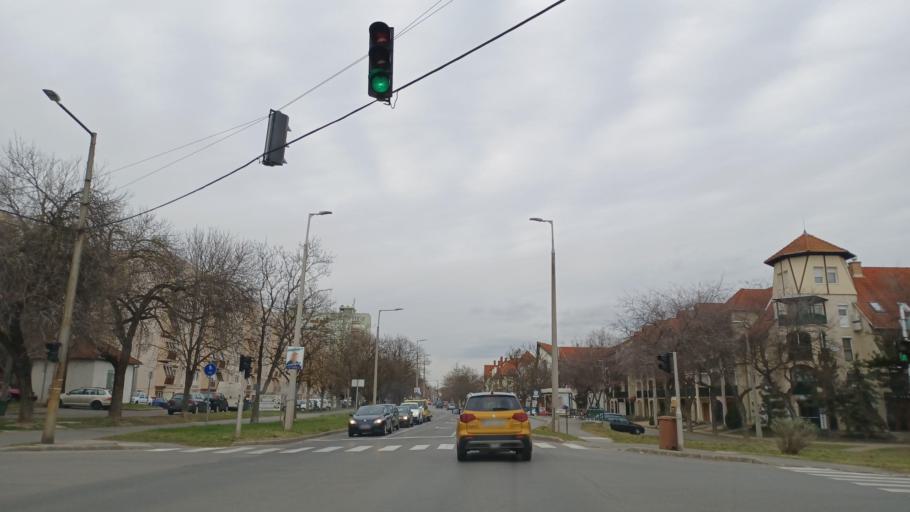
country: HU
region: Tolna
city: Szekszard
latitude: 46.3376
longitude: 18.7009
